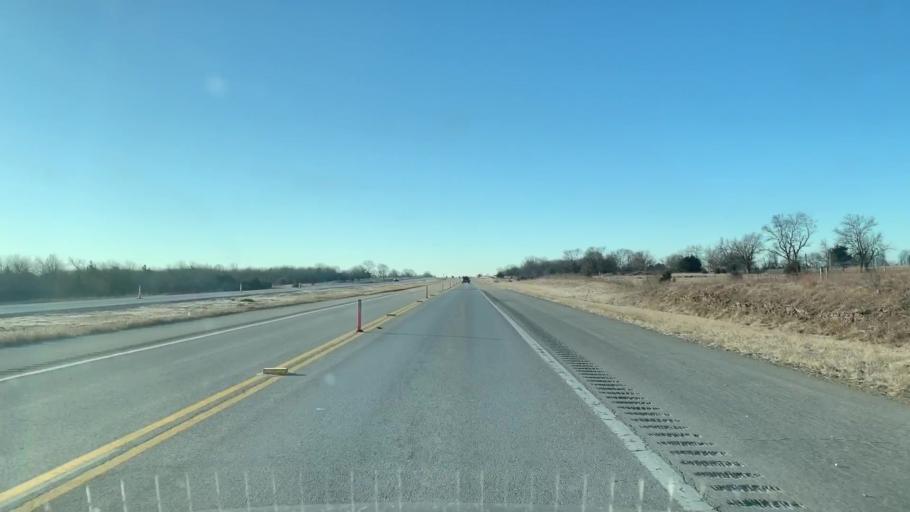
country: US
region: Kansas
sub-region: Bourbon County
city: Fort Scott
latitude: 37.7594
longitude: -94.7050
